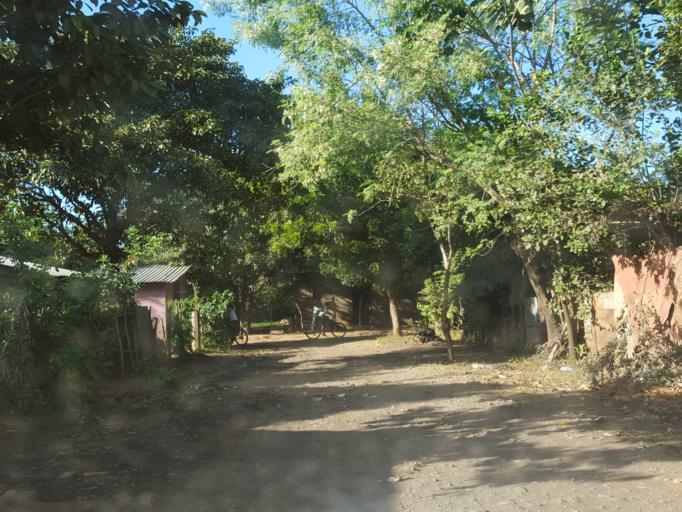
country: NI
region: Leon
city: Leon
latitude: 12.4264
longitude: -86.9094
